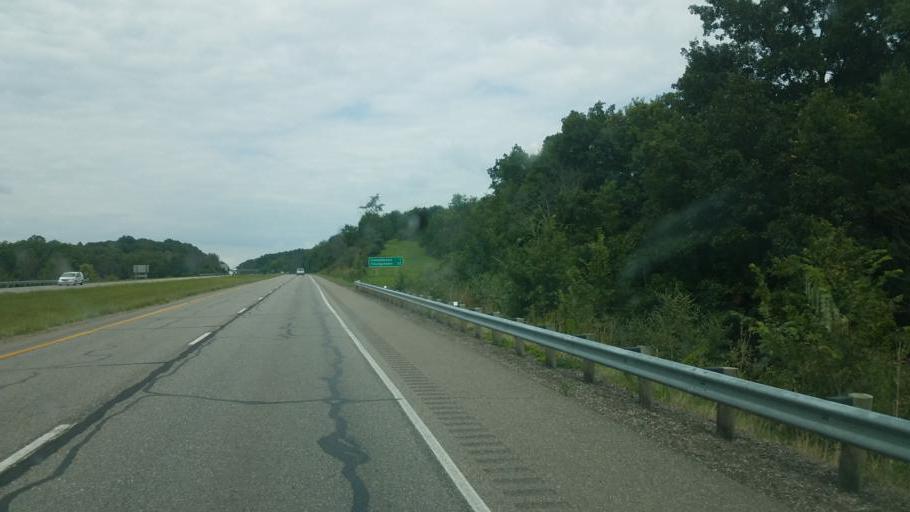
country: US
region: Ohio
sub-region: Columbiana County
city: Lisbon
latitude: 40.7774
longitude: -80.7345
